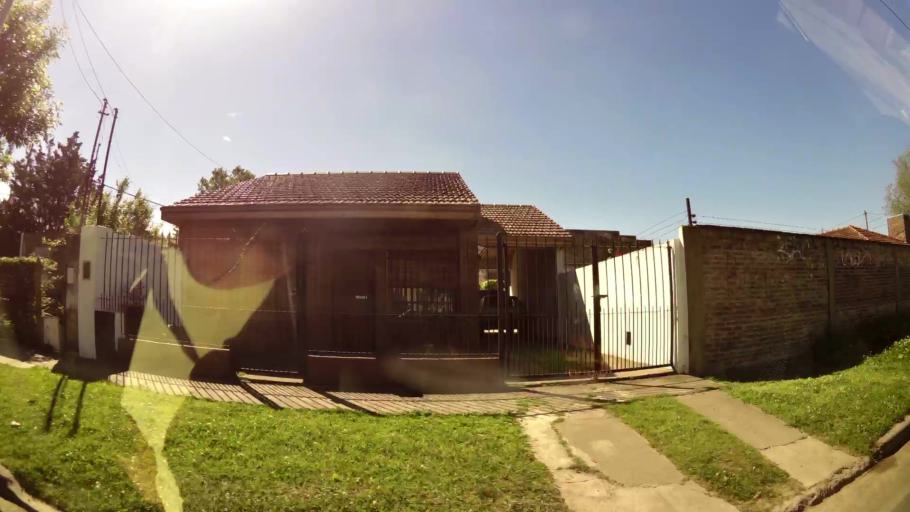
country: AR
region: Buenos Aires
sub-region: Partido de Almirante Brown
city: Adrogue
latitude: -34.7892
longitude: -58.3620
